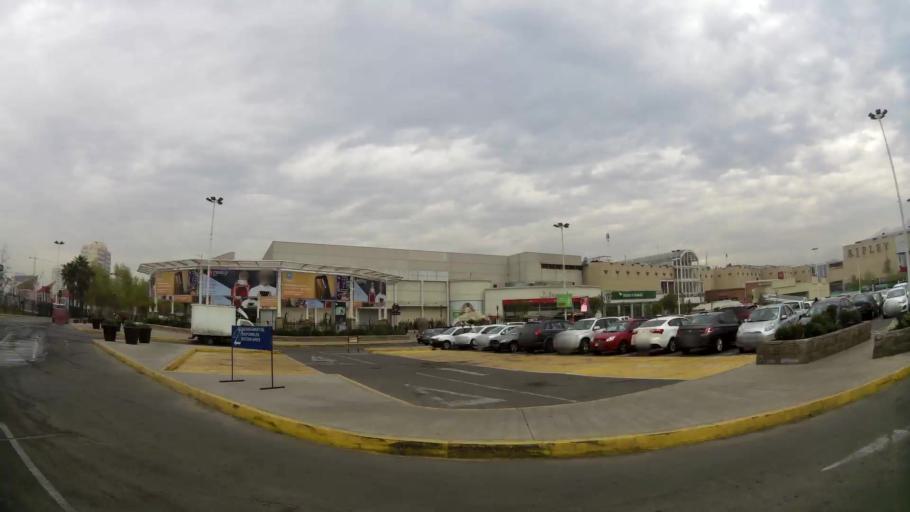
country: CL
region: Santiago Metropolitan
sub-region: Provincia de Santiago
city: Villa Presidente Frei, Nunoa, Santiago, Chile
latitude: -33.5194
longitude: -70.5993
